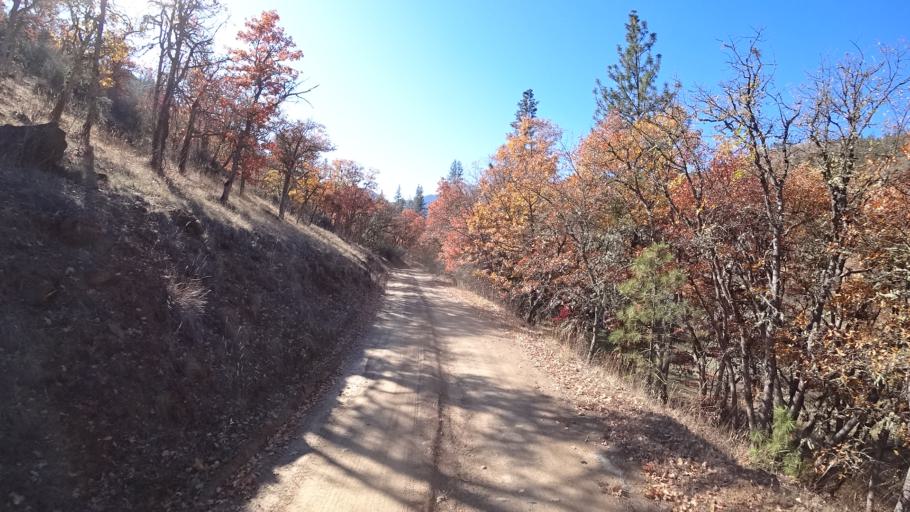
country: US
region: California
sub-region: Siskiyou County
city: Yreka
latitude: 41.8655
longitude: -122.7428
